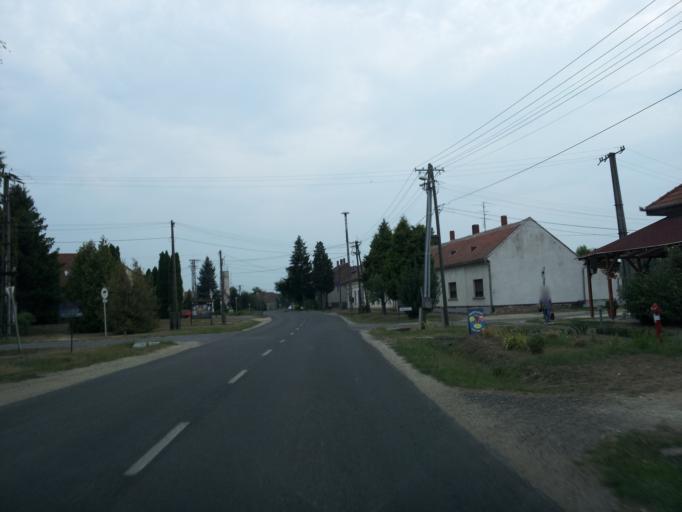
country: HU
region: Vas
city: Sarvar
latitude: 47.2059
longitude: 16.8939
